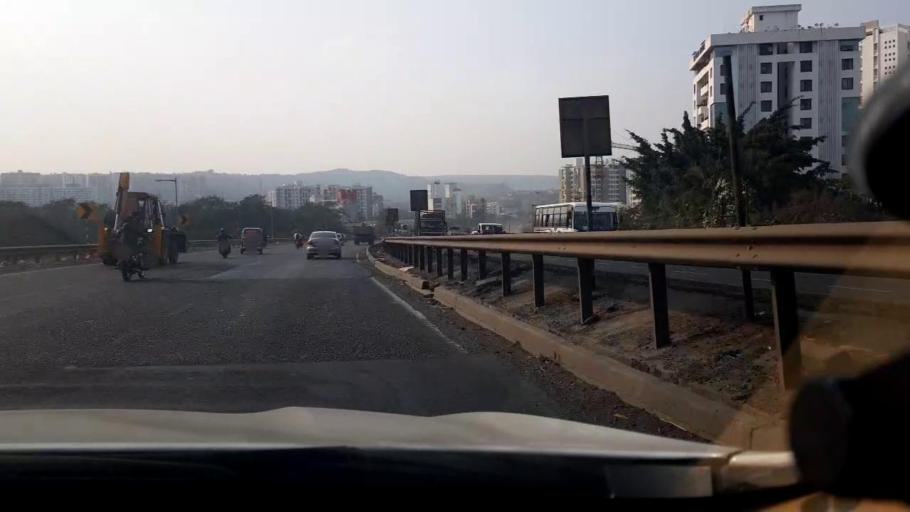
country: IN
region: Maharashtra
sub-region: Pune Division
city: Kharakvasla
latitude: 18.5092
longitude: 73.7748
